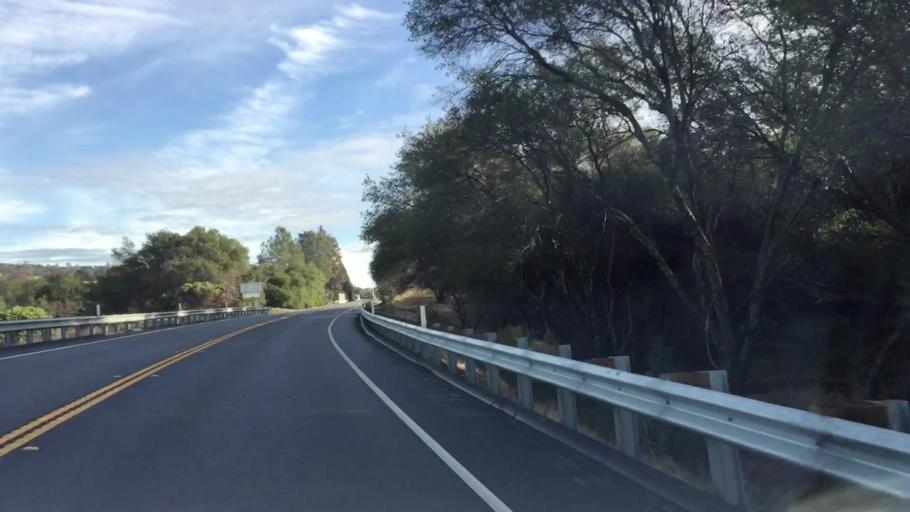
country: US
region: California
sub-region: Butte County
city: Paradise
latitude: 39.6513
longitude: -121.5569
